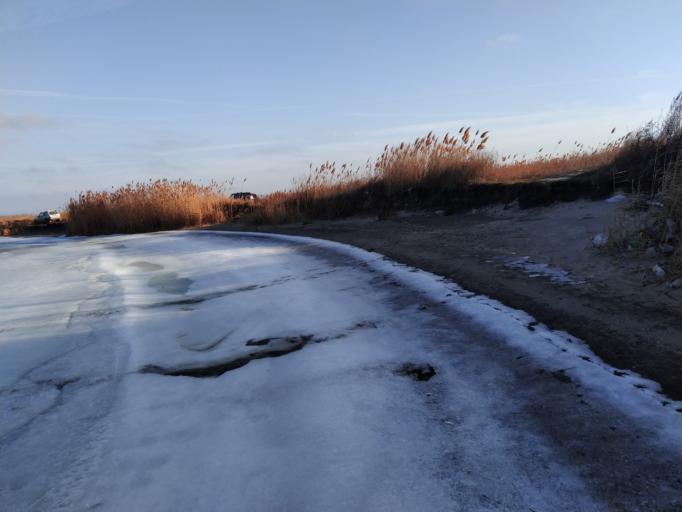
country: RU
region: Rostov
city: Bataysk
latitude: 47.1438
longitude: 39.6602
